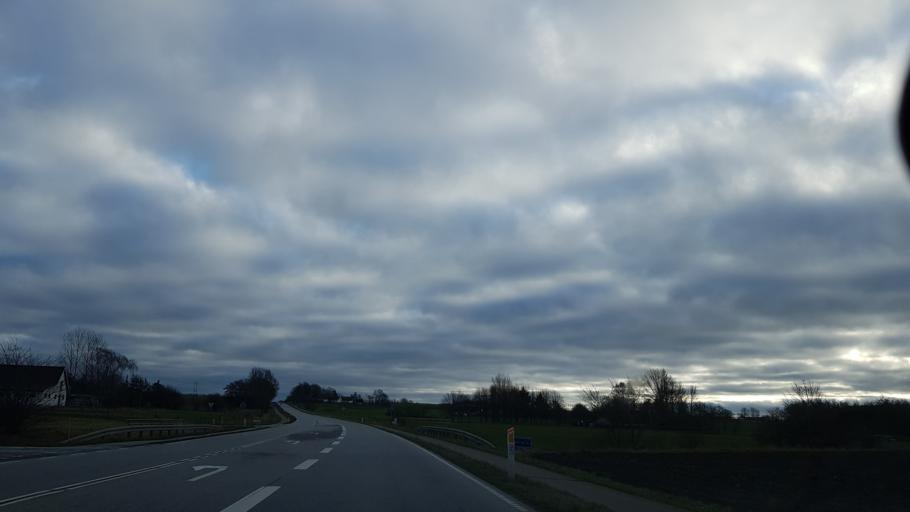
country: DK
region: Zealand
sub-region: Kalundborg Kommune
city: Hong
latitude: 55.5028
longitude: 11.2668
